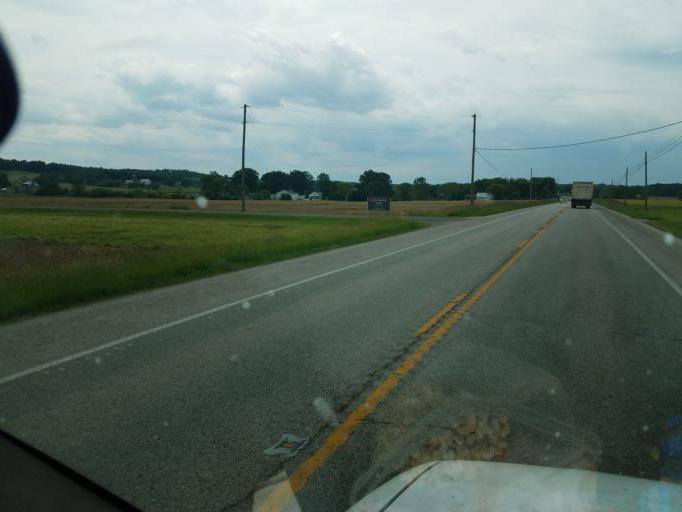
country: US
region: Ohio
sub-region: Wayne County
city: Apple Creek
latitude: 40.7563
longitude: -81.8581
